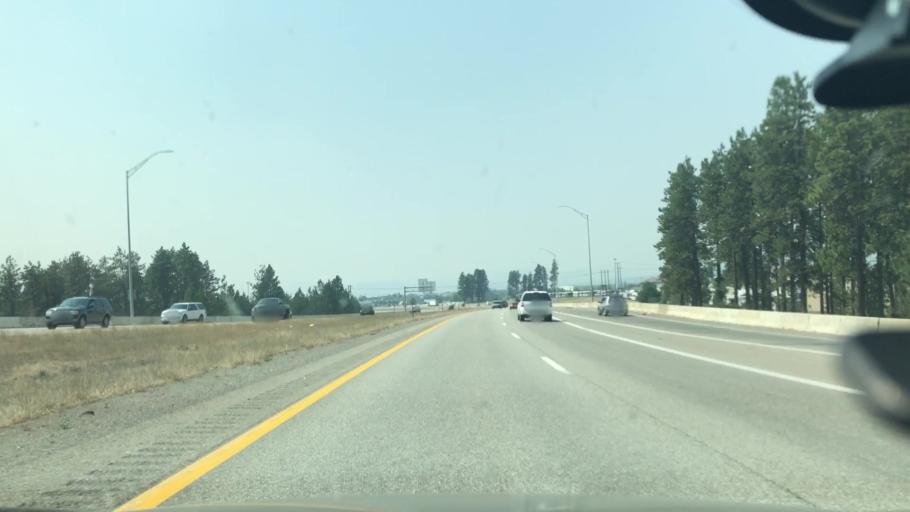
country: US
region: Idaho
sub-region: Kootenai County
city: Post Falls
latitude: 47.7130
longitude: -116.9532
